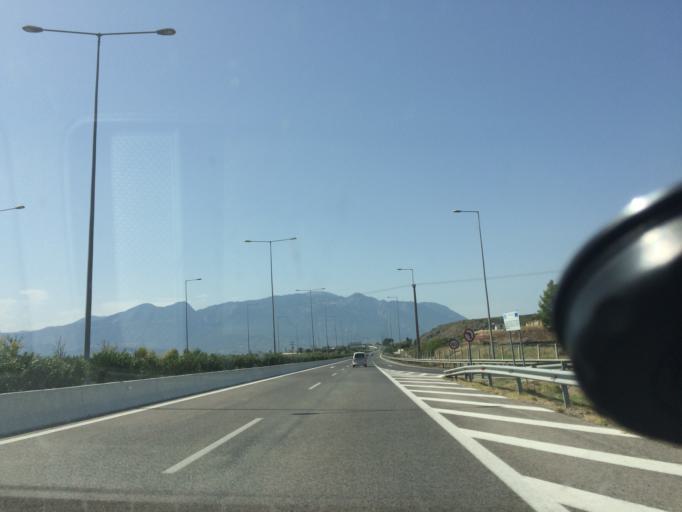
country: GR
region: Central Greece
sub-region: Nomos Fthiotidos
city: Rodhitsa
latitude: 38.8986
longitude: 22.4994
